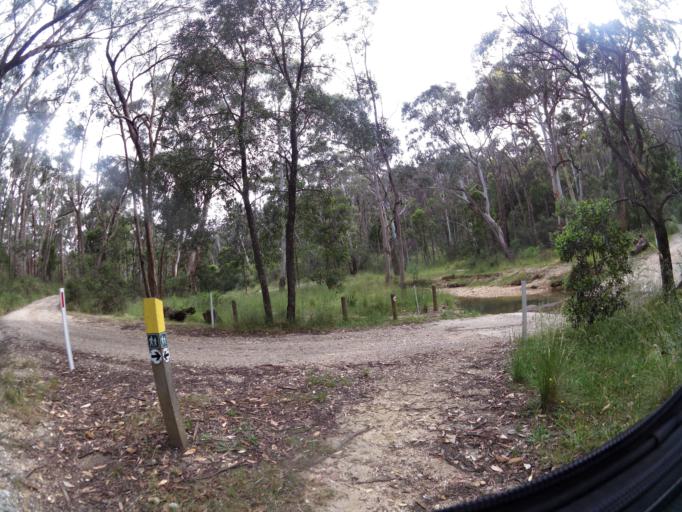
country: AU
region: Victoria
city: Brown Hill
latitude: -37.4673
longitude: 143.9082
